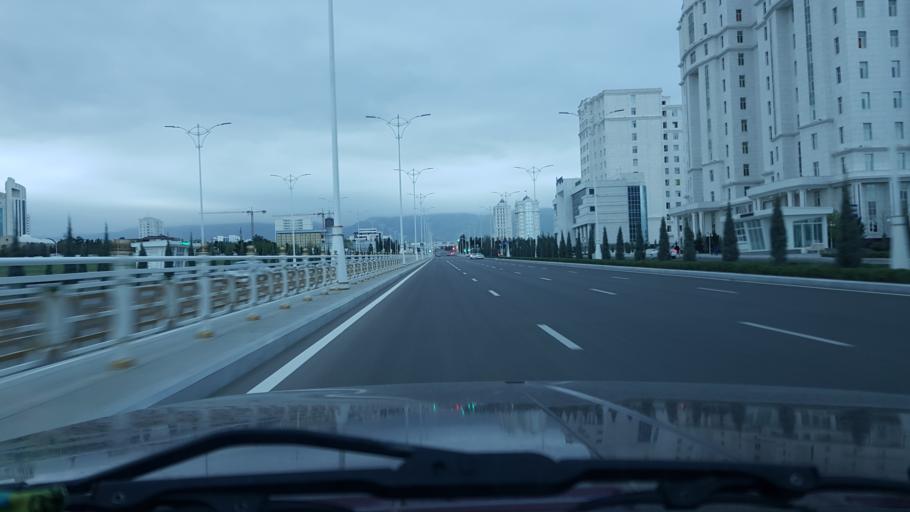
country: TM
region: Ahal
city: Ashgabat
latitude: 37.8887
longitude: 58.3631
